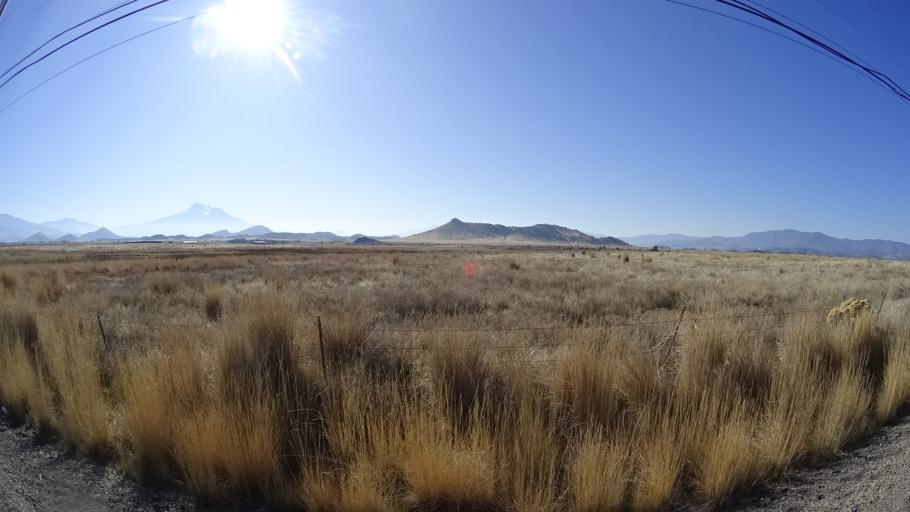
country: US
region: California
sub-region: Siskiyou County
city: Montague
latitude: 41.7266
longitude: -122.4624
